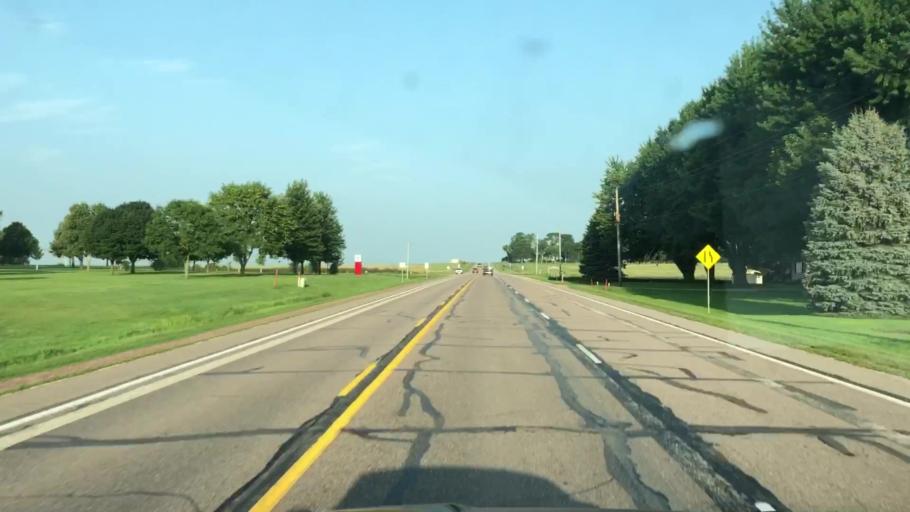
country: US
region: Iowa
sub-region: O'Brien County
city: Sheldon
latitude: 43.1859
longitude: -95.8794
